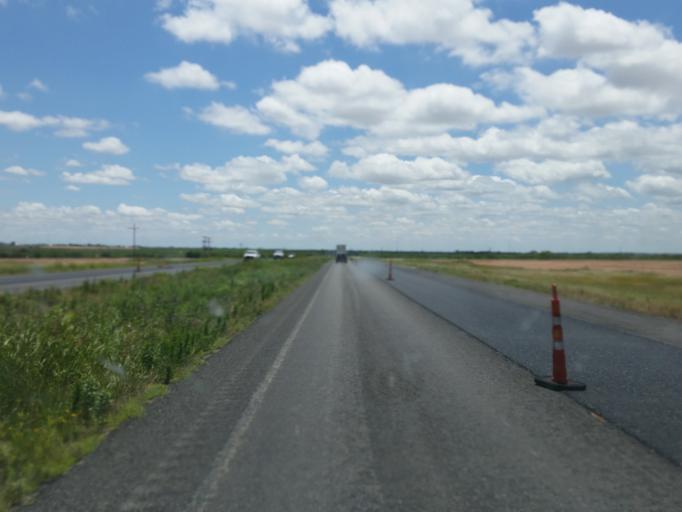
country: US
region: Texas
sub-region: Scurry County
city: Snyder
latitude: 32.7754
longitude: -100.9415
